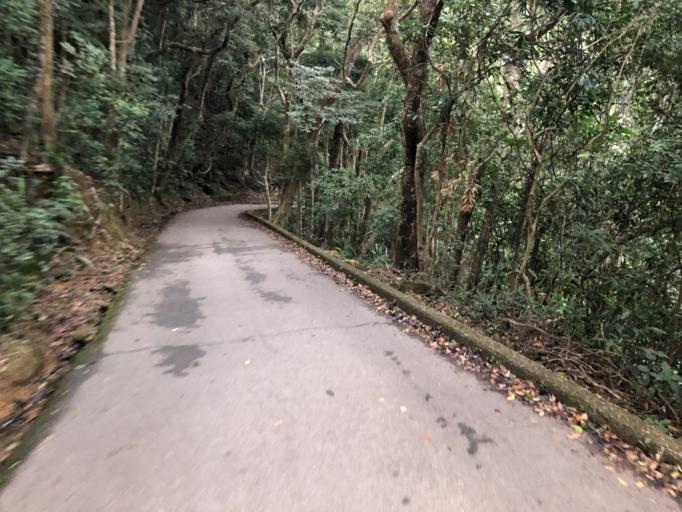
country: HK
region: Wanchai
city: Wan Chai
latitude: 22.2658
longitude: 114.2138
